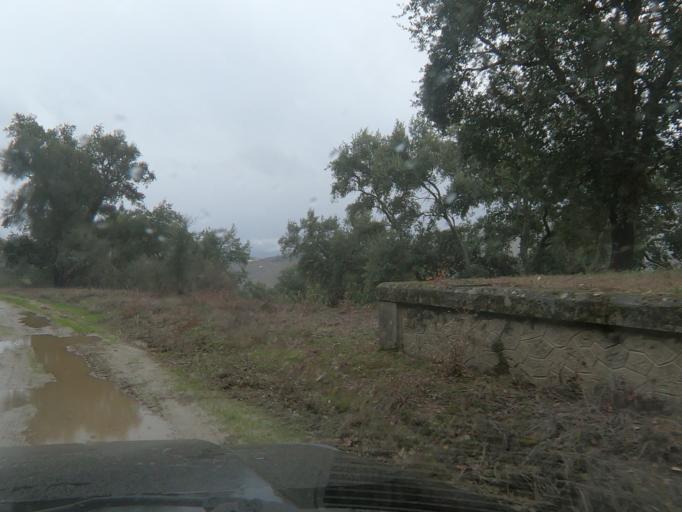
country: PT
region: Vila Real
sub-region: Vila Real
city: Vila Real
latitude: 41.2496
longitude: -7.7472
